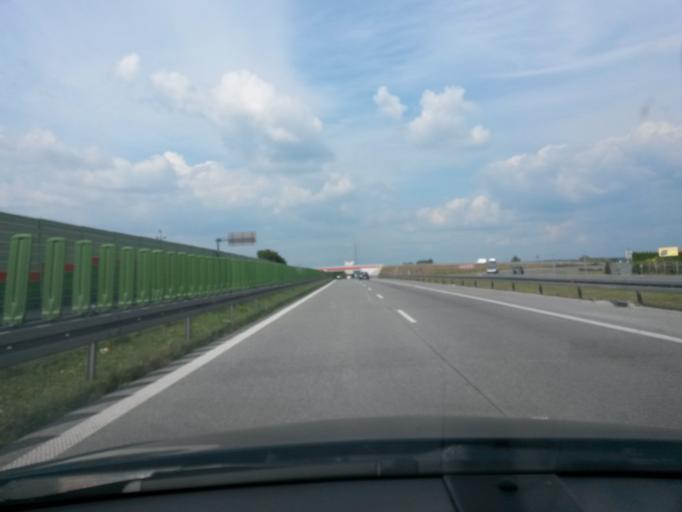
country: PL
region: Lodz Voivodeship
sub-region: Powiat rawski
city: Rawa Mazowiecka
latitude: 51.7539
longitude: 20.2537
